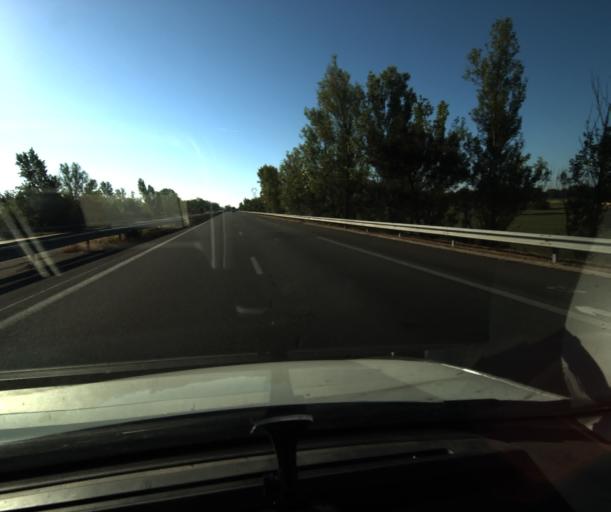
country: FR
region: Midi-Pyrenees
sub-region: Departement du Tarn-et-Garonne
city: Montech
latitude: 43.9836
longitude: 1.2477
